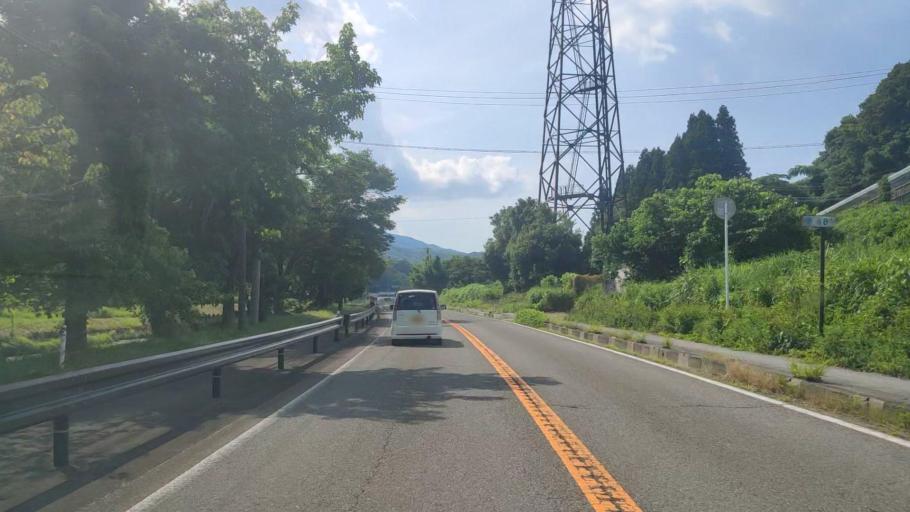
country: JP
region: Fukui
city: Tsuruga
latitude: 35.5510
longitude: 136.1460
